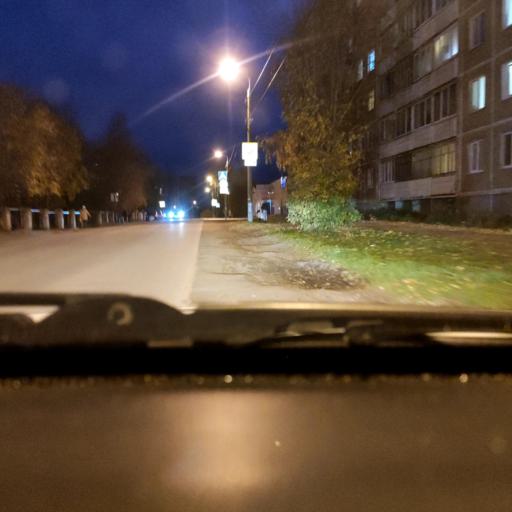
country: RU
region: Perm
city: Perm
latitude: 58.1005
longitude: 56.3013
